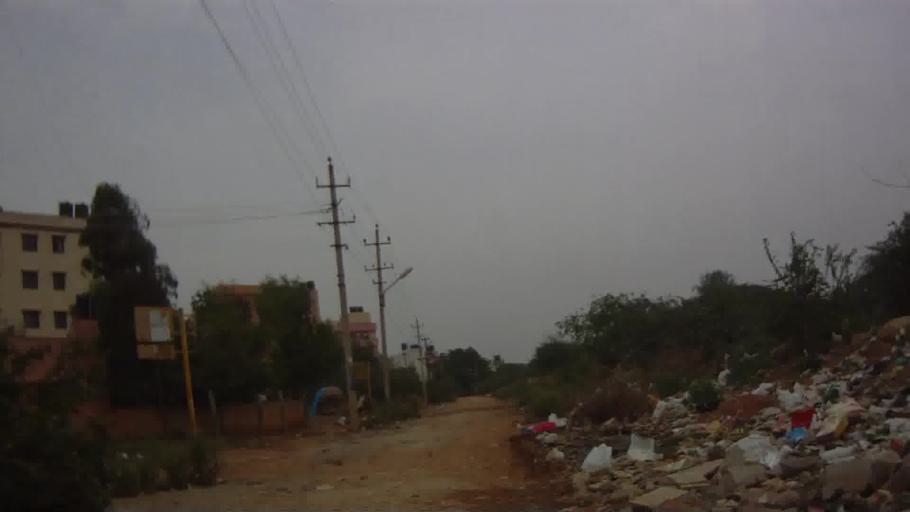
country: IN
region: Karnataka
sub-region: Bangalore Urban
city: Bangalore
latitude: 12.9701
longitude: 77.7024
